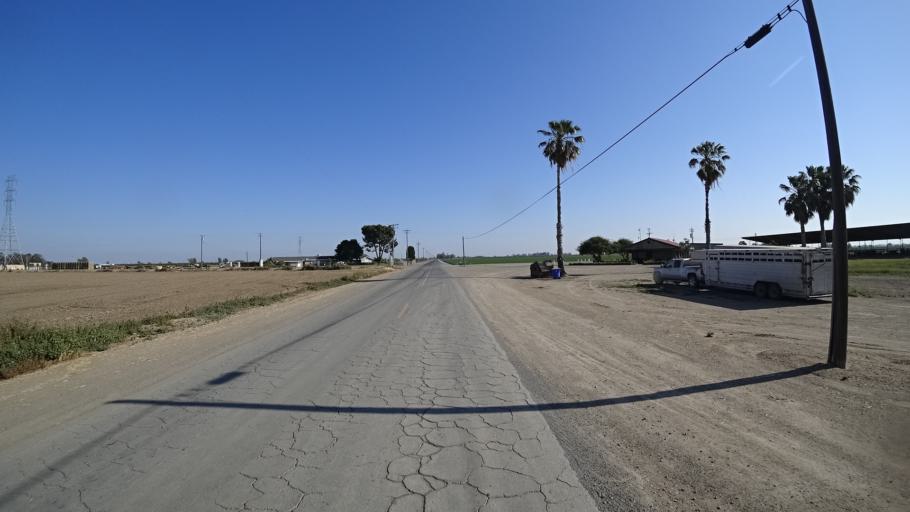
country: US
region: California
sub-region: Fresno County
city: Riverdale
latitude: 36.3500
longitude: -119.8872
